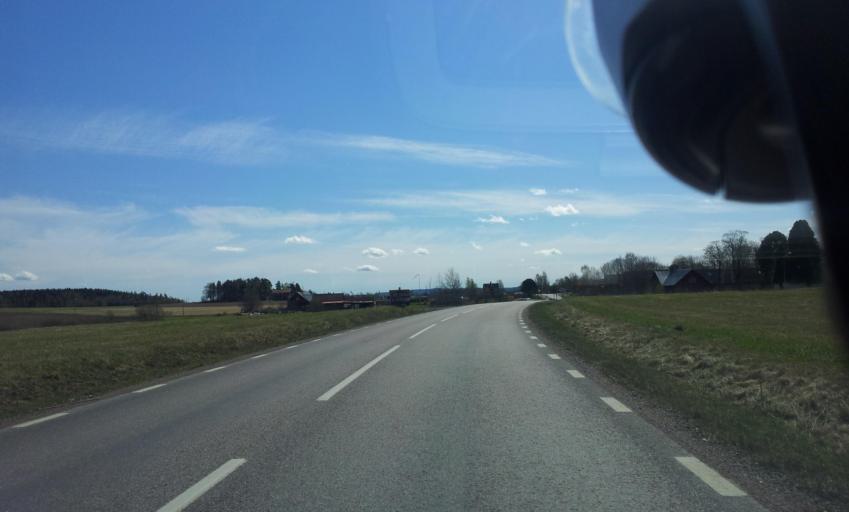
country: SE
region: Dalarna
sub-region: Borlange Kommun
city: Ornas
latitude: 60.4755
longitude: 15.5032
